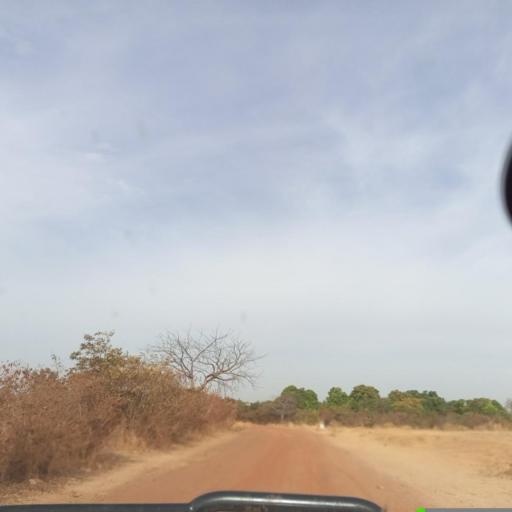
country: ML
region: Koulikoro
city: Koulikoro
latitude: 13.1079
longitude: -7.6478
